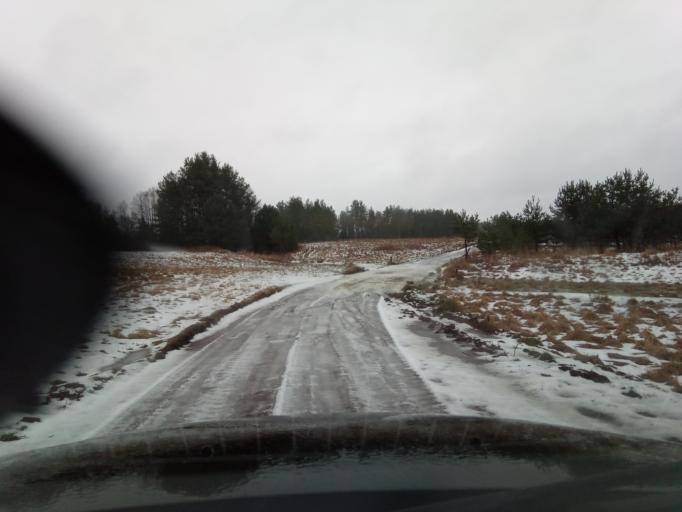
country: LT
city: Svencioneliai
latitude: 55.3377
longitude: 25.8075
